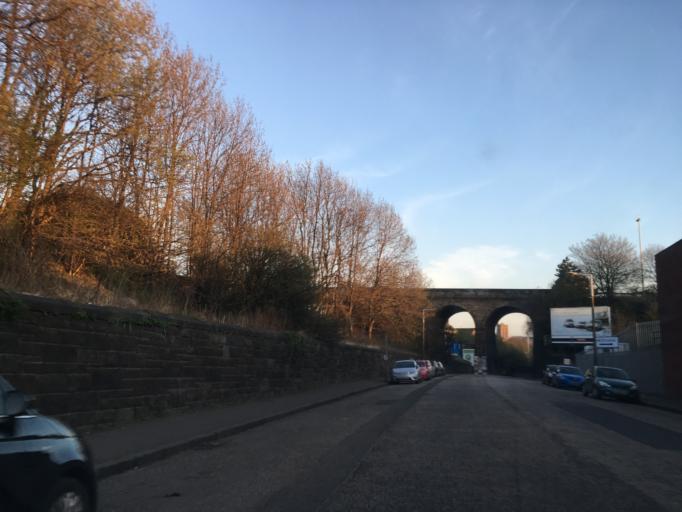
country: GB
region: Scotland
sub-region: Edinburgh
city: Edinburgh
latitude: 55.9421
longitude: -3.2287
